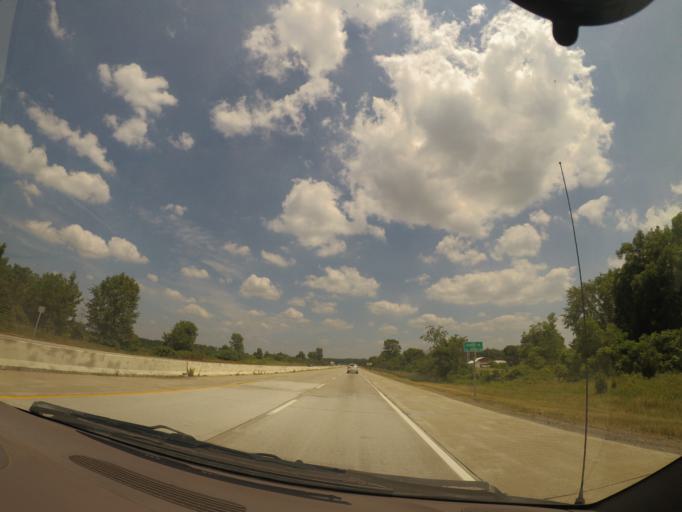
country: US
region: Indiana
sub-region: Saint Joseph County
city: Osceola
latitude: 41.6161
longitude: -86.0613
